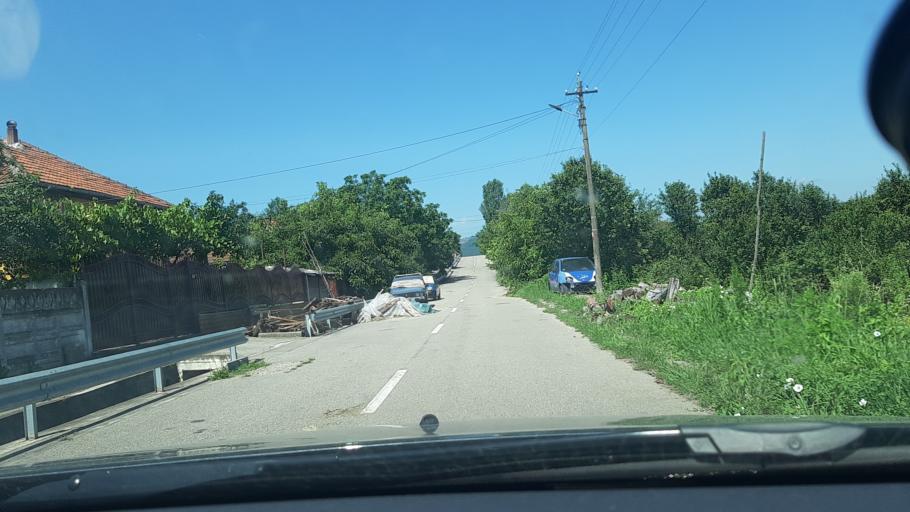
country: RO
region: Hunedoara
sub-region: Comuna Teliucu Inferior
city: Teliucu Inferior
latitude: 45.7024
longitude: 22.8936
